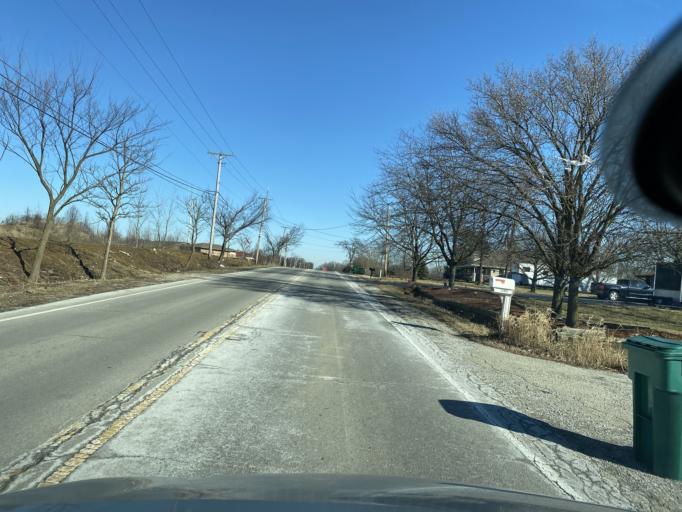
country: US
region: Illinois
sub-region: Cook County
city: Lemont
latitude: 41.6546
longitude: -87.9768
